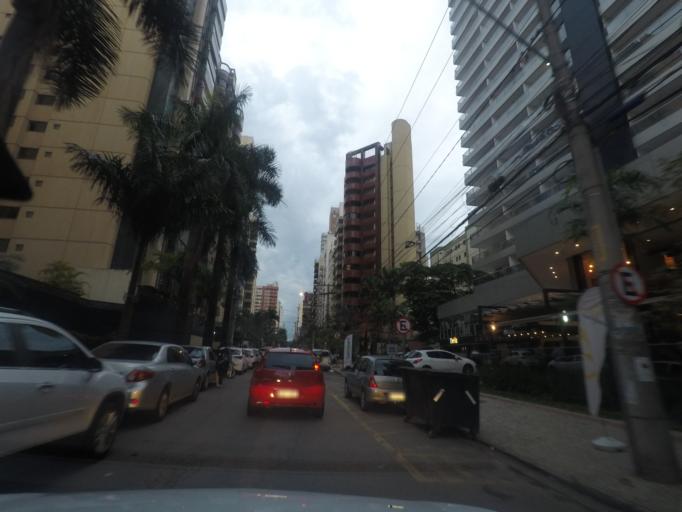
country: BR
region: Goias
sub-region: Goiania
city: Goiania
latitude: -16.7103
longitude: -49.2660
